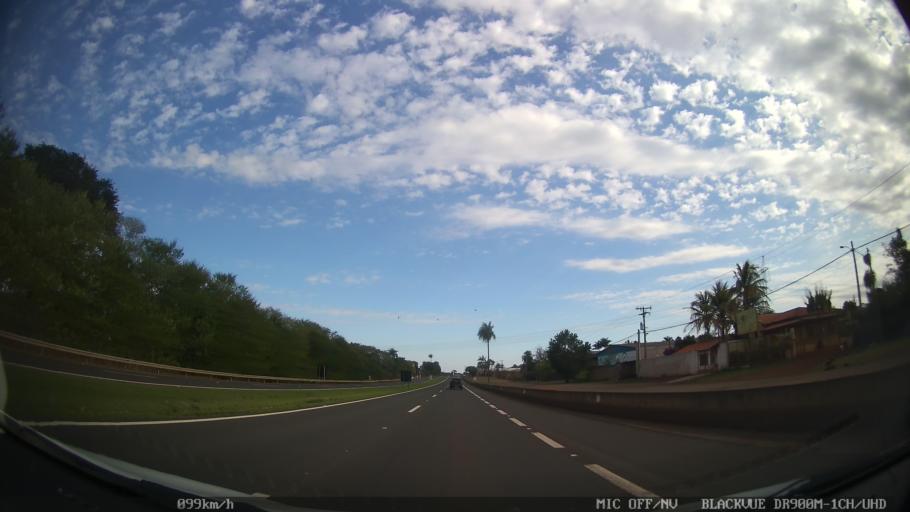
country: BR
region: Sao Paulo
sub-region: Iracemapolis
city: Iracemapolis
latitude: -22.5945
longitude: -47.4666
